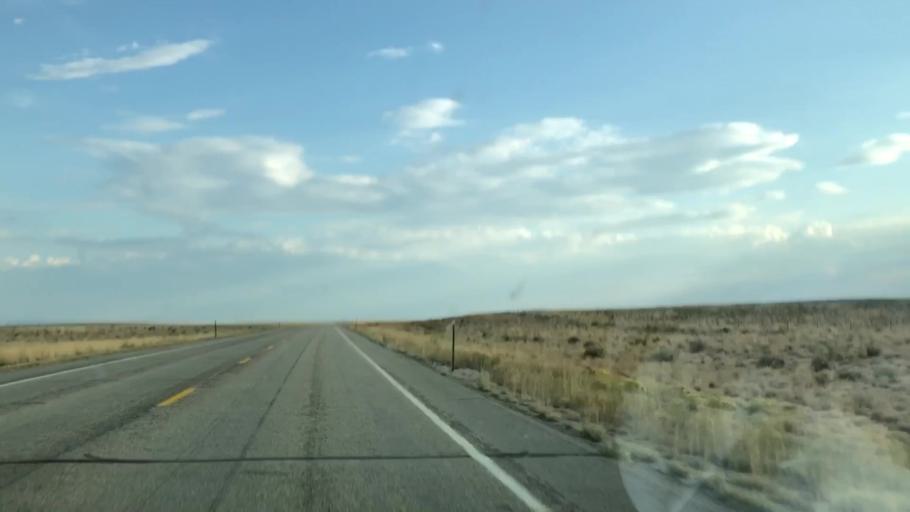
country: US
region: Wyoming
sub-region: Sweetwater County
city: North Rock Springs
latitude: 42.2511
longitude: -109.4672
